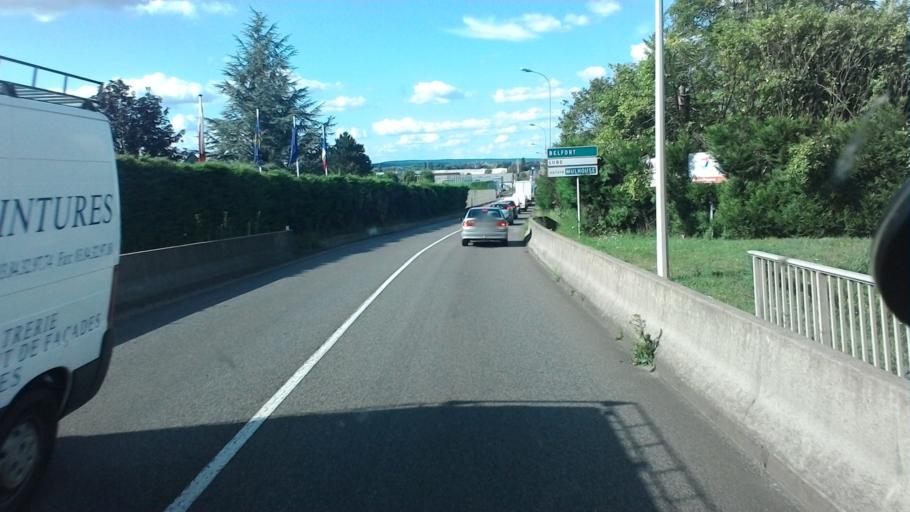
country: FR
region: Franche-Comte
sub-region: Departement de la Haute-Saone
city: Noidans-les-Vesoul
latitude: 47.6145
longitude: 6.1331
